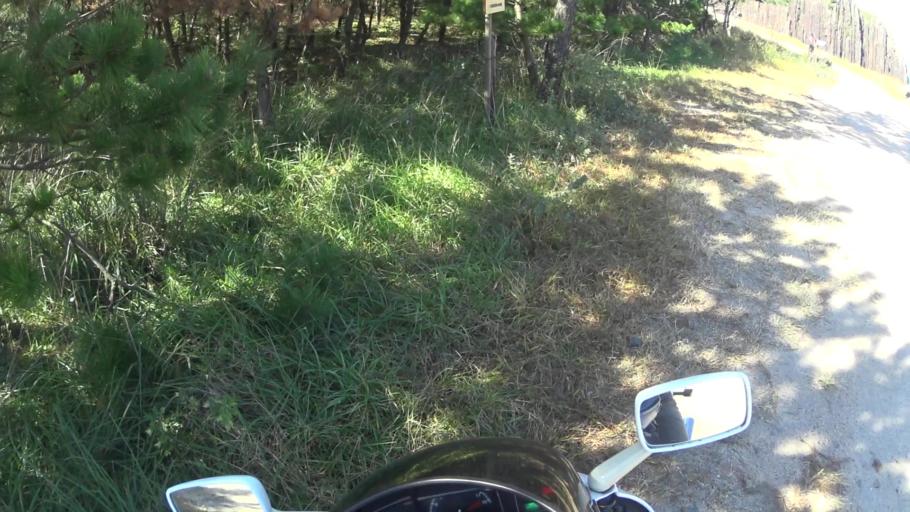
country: JP
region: Kyoto
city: Miyazu
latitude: 35.7423
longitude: 135.1060
